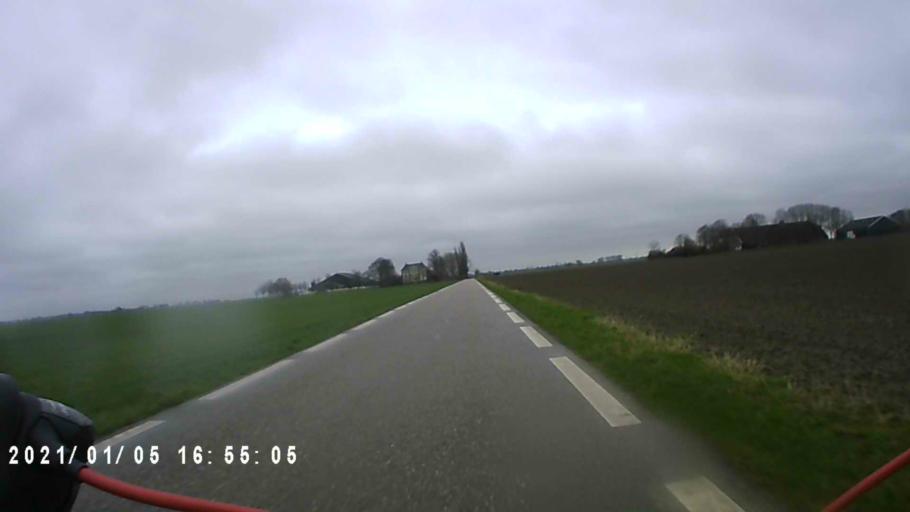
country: NL
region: Groningen
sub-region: Gemeente  Oldambt
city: Winschoten
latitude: 53.2426
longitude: 7.0553
